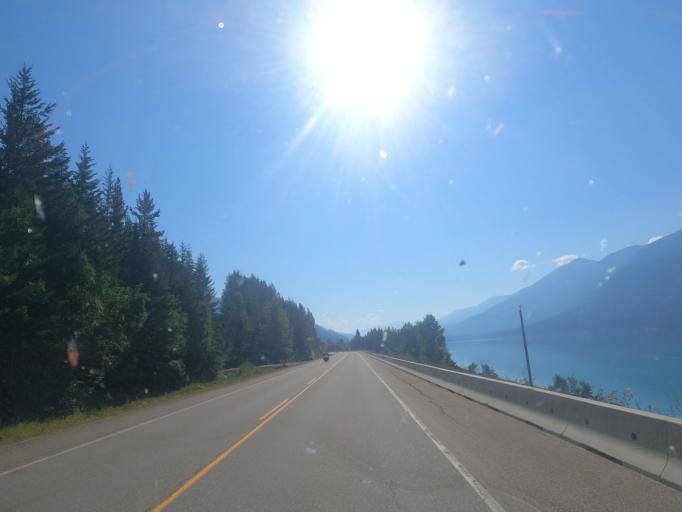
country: CA
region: Alberta
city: Jasper Park Lodge
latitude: 52.9574
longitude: -118.8974
